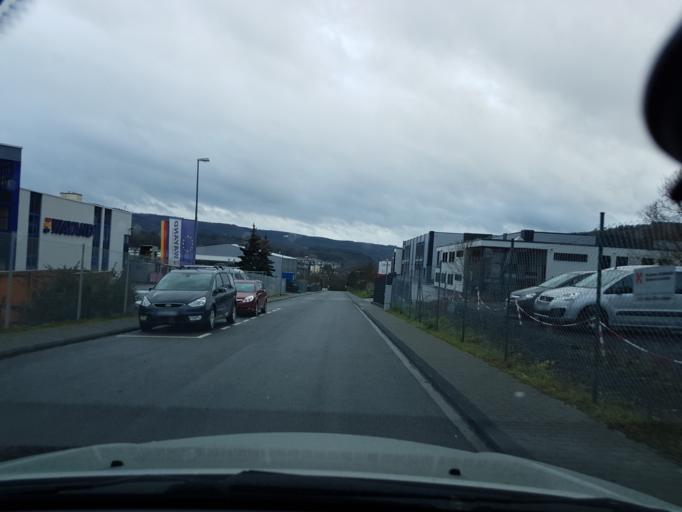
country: DE
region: Rheinland-Pfalz
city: Fischbach
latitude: 49.7252
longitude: 7.3772
